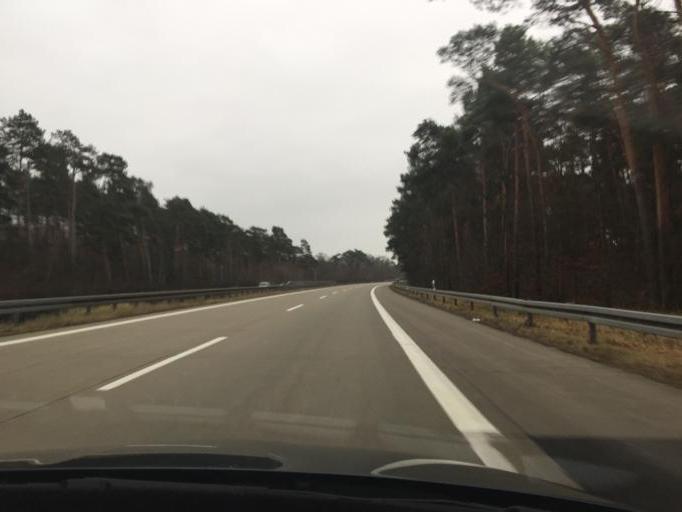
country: DE
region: Brandenburg
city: Lubbenau
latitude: 51.8263
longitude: 14.0020
